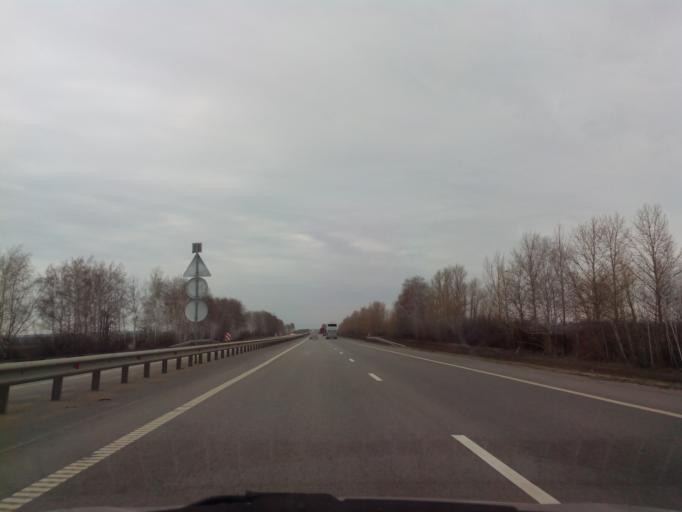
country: RU
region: Tambov
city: Selezni
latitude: 52.8089
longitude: 40.9602
